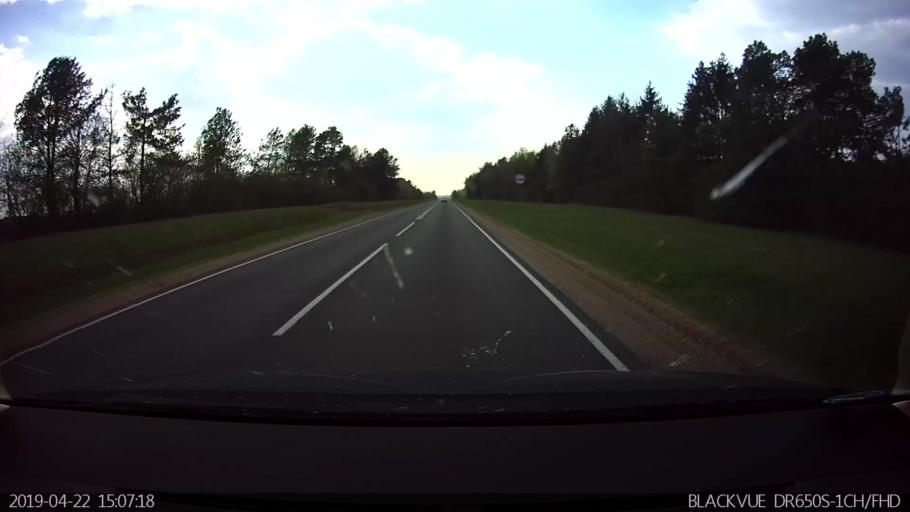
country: BY
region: Brest
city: Kamyanyets
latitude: 52.3290
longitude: 23.8117
